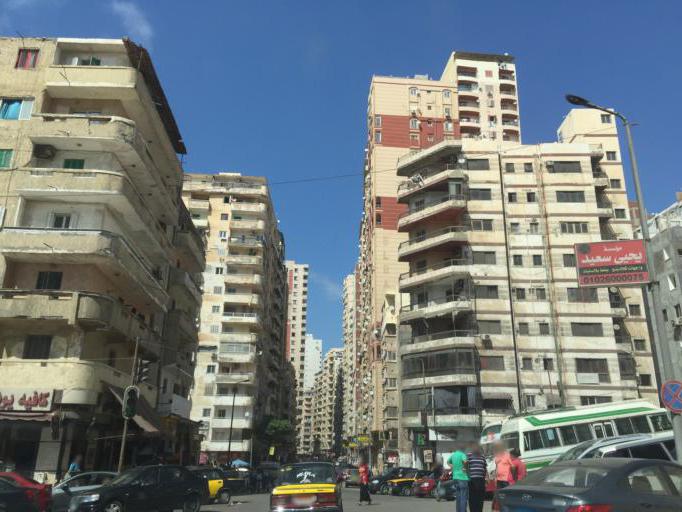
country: EG
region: Alexandria
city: Alexandria
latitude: 31.2619
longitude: 29.9850
